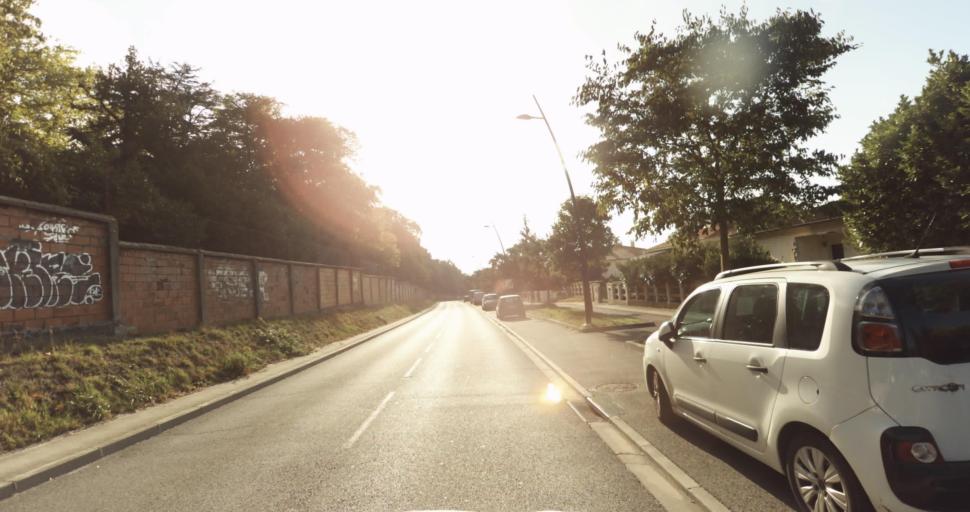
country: FR
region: Midi-Pyrenees
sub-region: Departement de la Haute-Garonne
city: Ramonville-Saint-Agne
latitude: 43.5396
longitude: 1.4640
